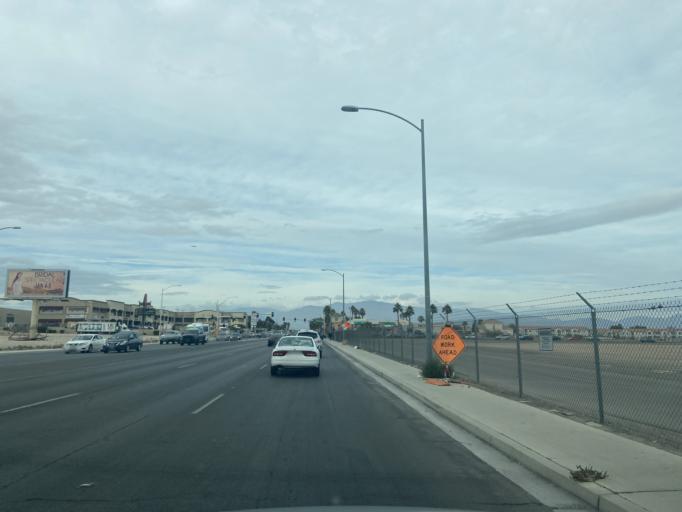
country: US
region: Nevada
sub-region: Clark County
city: Las Vegas
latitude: 36.2158
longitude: -115.2074
